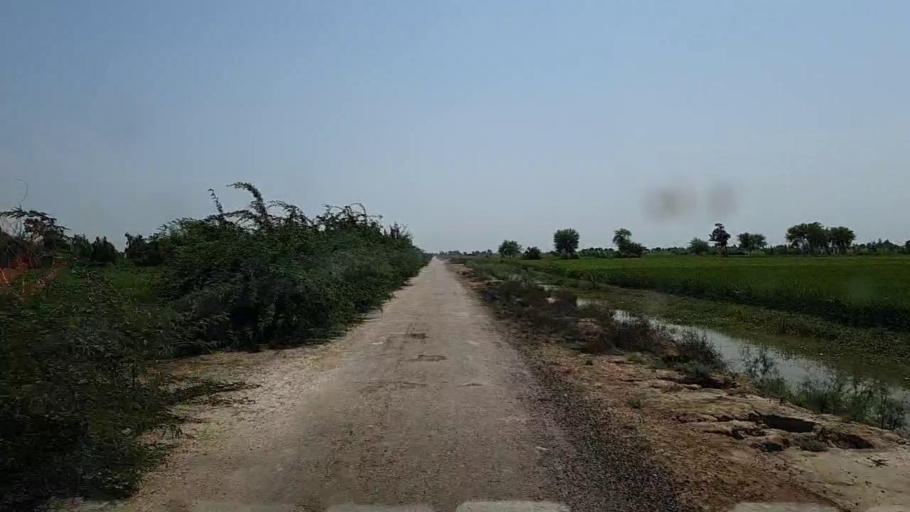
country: PK
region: Sindh
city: Mirpur Batoro
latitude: 24.6123
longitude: 68.4523
